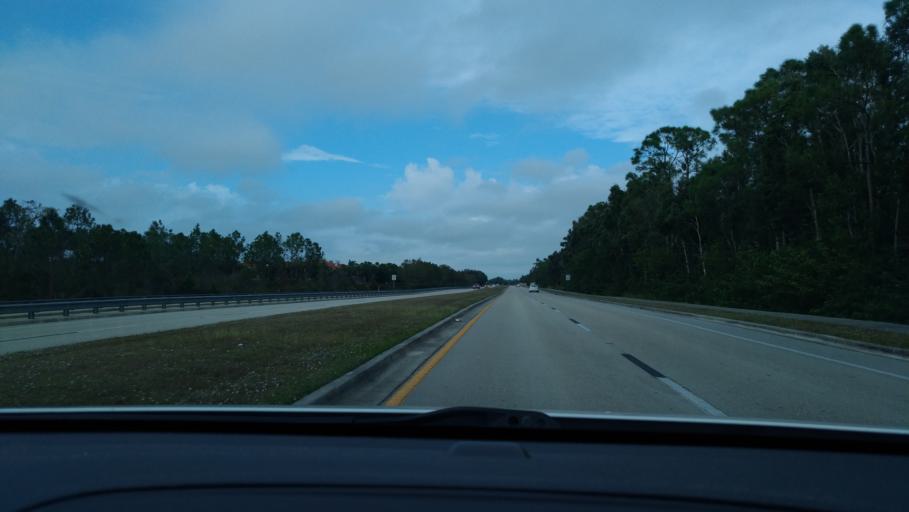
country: US
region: Florida
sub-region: Lee County
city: Estero
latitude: 26.4088
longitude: -81.8046
